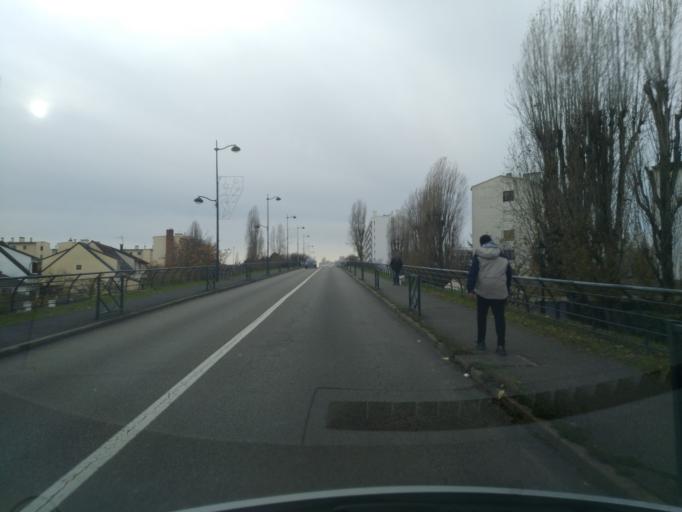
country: FR
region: Ile-de-France
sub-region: Departement des Yvelines
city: Villepreux
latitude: 48.8278
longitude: 1.9907
